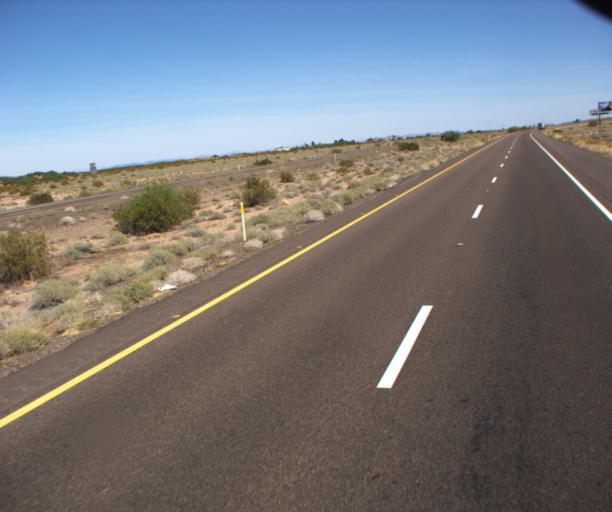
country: US
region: Arizona
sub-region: Yuma County
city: Wellton
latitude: 32.7955
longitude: -113.5505
